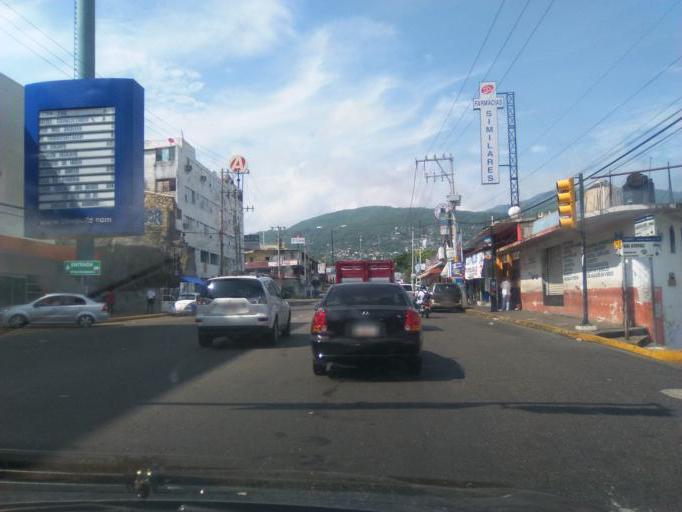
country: MX
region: Guerrero
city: Acapulco de Juarez
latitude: 16.8582
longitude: -99.9151
